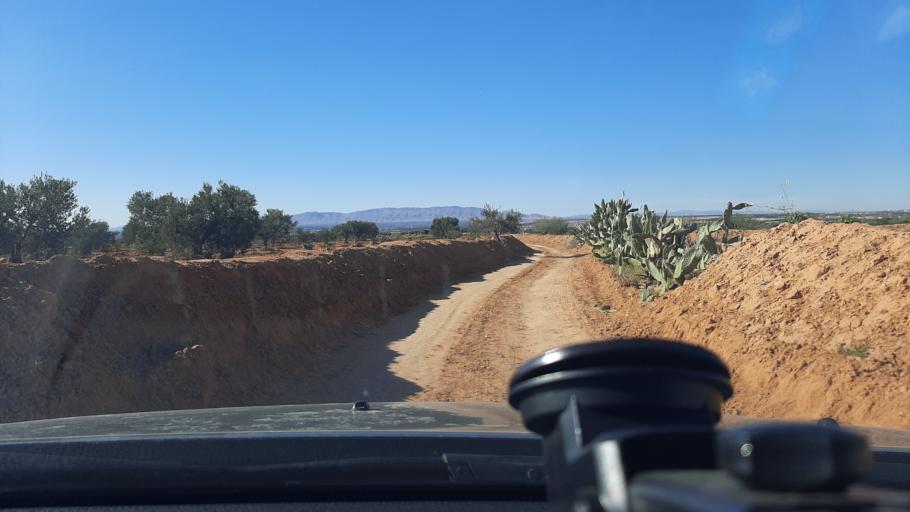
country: TN
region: Safaqis
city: Bi'r `Ali Bin Khalifah
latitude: 34.9995
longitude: 10.0882
